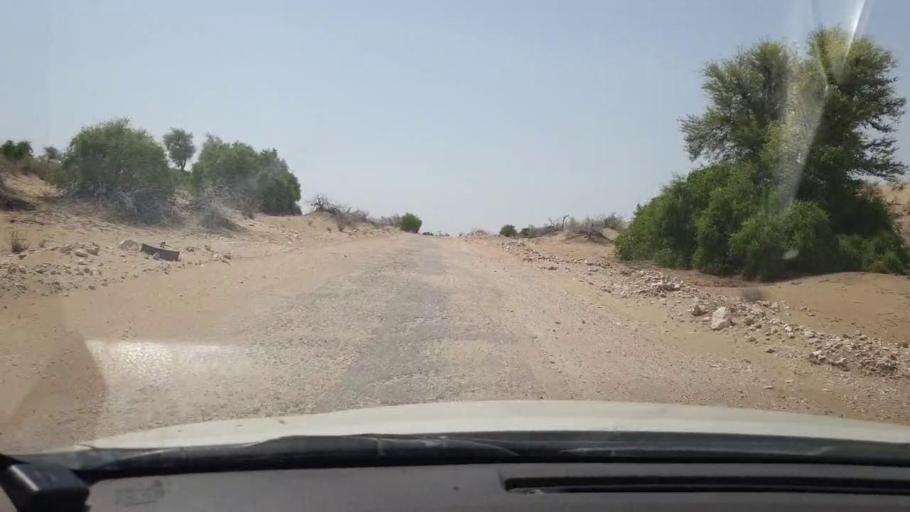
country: PK
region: Sindh
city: Rohri
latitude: 27.3204
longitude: 69.2776
